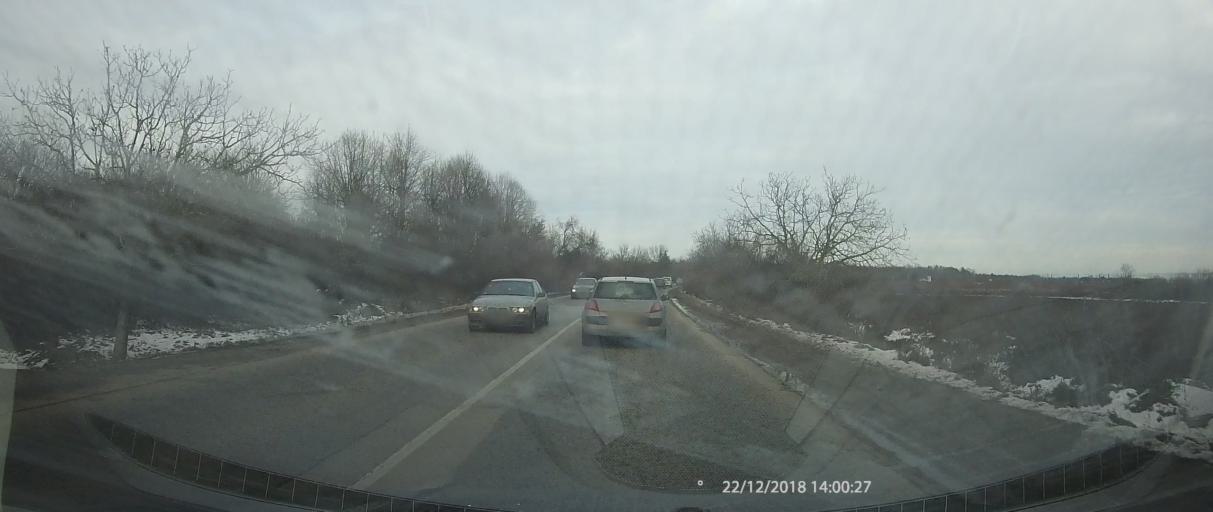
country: BG
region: Pleven
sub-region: Obshtina Dolni Dubnik
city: Dolni Dubnik
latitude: 43.3620
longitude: 24.3437
